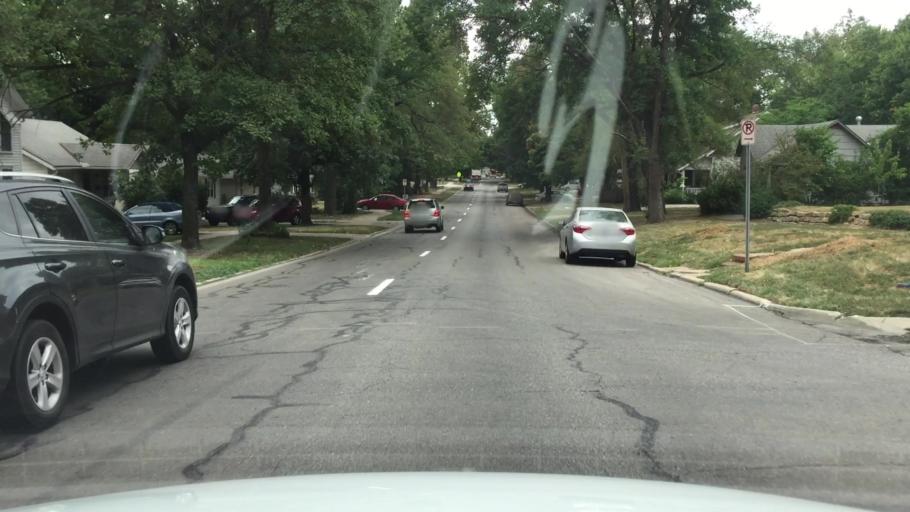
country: US
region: Kansas
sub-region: Douglas County
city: Lawrence
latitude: 38.9536
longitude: -95.2394
